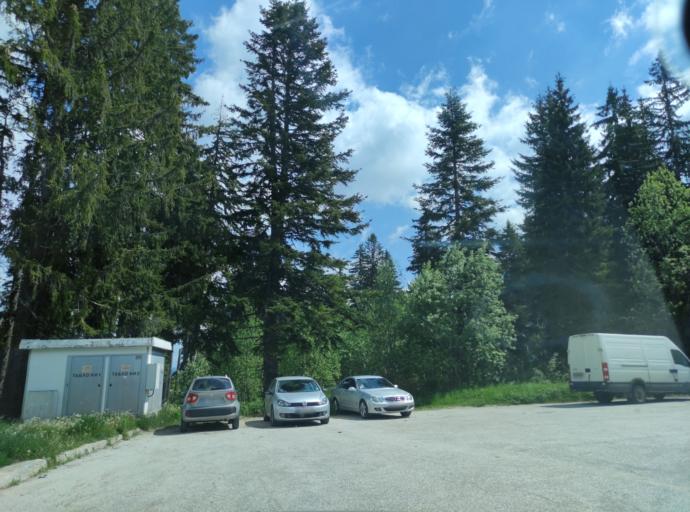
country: BG
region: Smolyan
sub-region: Obshtina Smolyan
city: Smolyan
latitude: 41.6484
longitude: 24.6967
